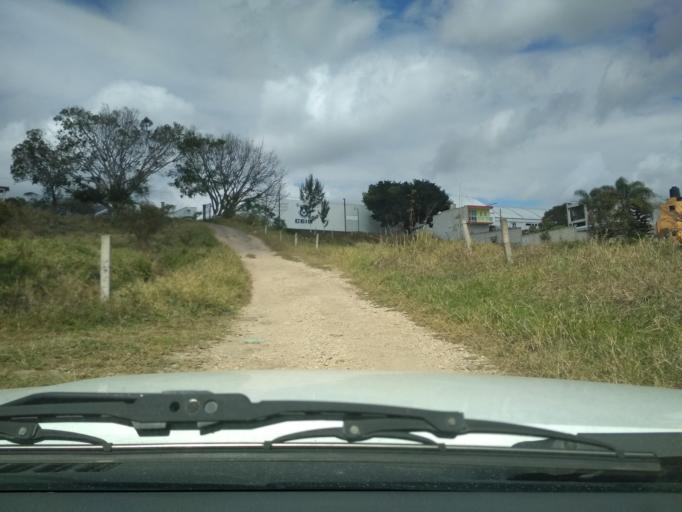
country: MX
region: Veracruz
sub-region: Emiliano Zapata
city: Dos Rios
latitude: 19.4844
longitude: -96.8103
